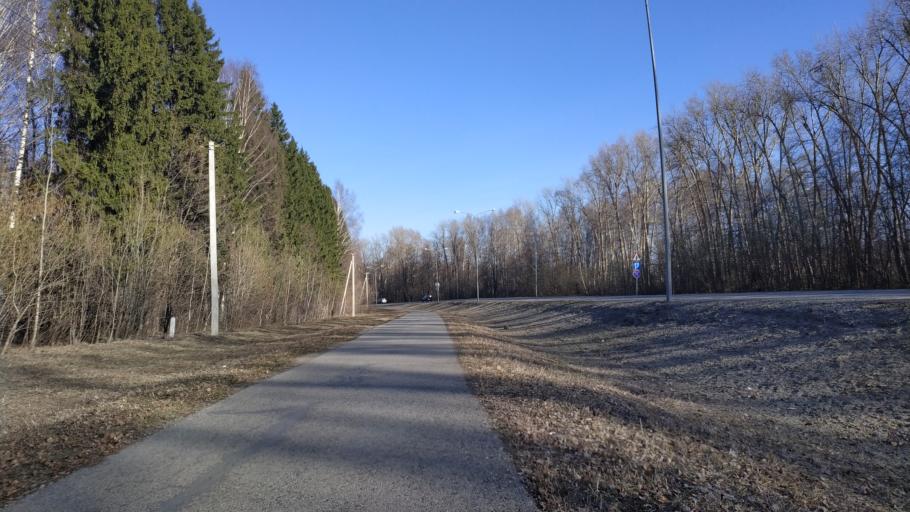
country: RU
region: Chuvashia
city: Novyye Lapsary
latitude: 56.1288
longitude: 47.1189
